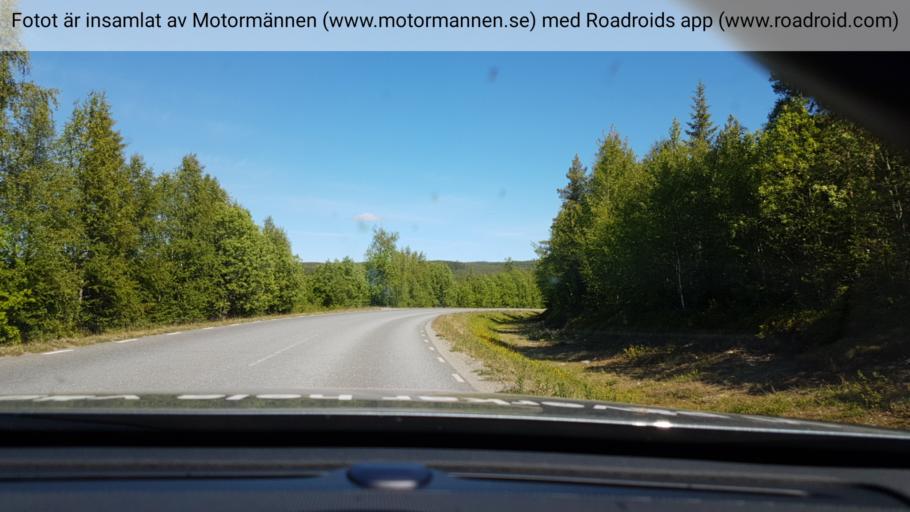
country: SE
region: Vaesterbotten
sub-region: Vilhelmina Kommun
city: Vilhelmina
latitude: 64.6495
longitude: 16.9814
